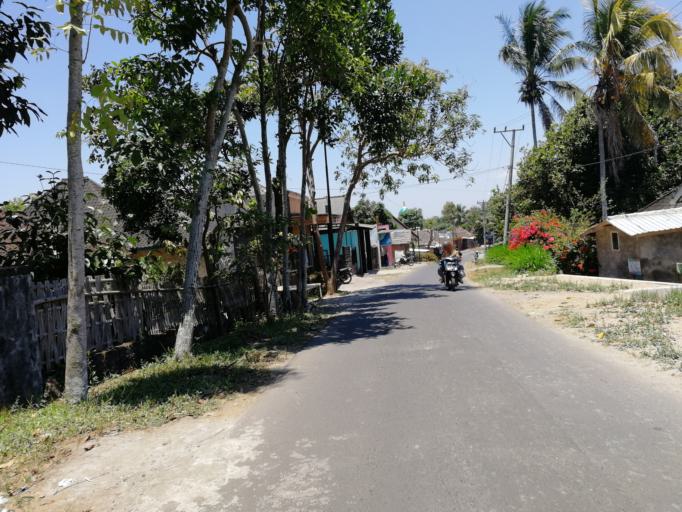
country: ID
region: West Nusa Tenggara
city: Tetebatu
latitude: -8.5604
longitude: 116.4197
